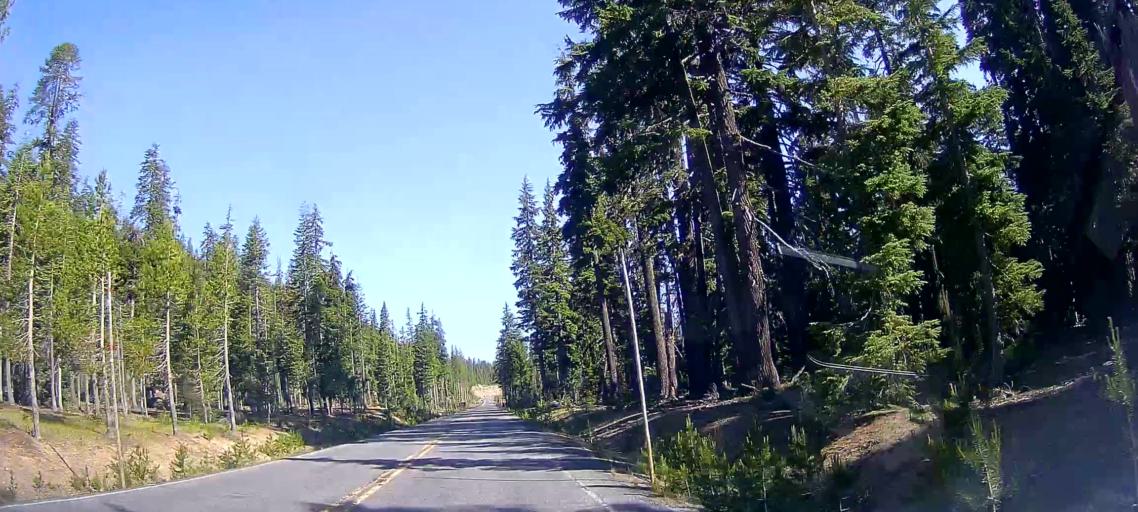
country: US
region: Oregon
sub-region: Jackson County
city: Shady Cove
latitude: 42.8618
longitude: -122.1661
